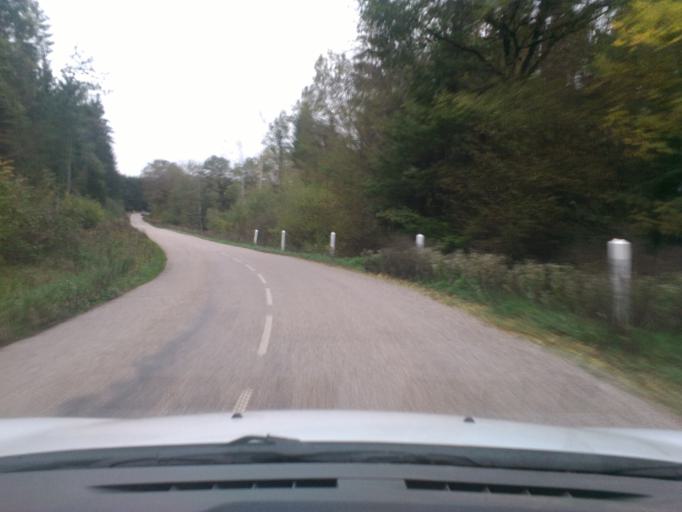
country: FR
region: Lorraine
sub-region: Departement des Vosges
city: Chavelot
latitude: 48.2845
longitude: 6.4582
